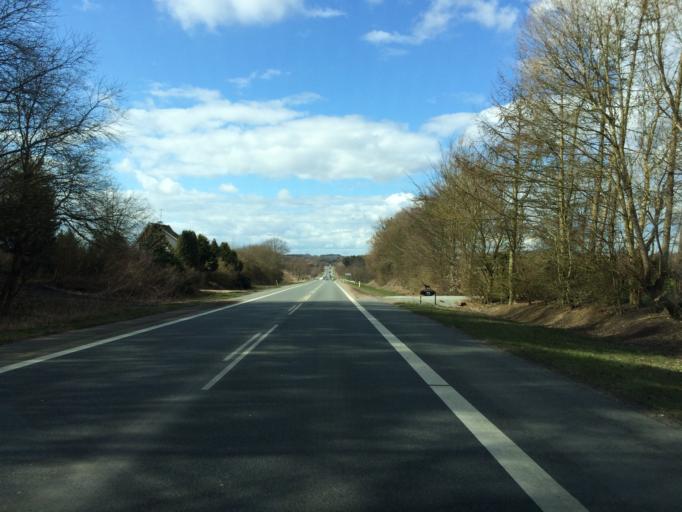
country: DK
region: South Denmark
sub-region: Assens Kommune
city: Vissenbjerg
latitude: 55.3956
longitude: 10.1041
